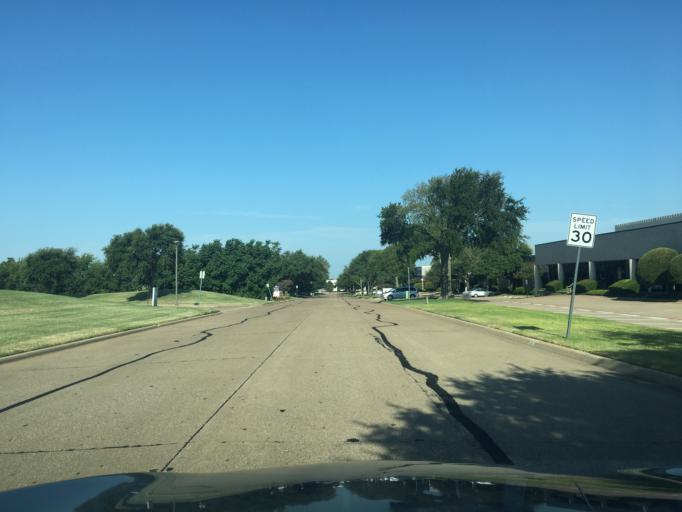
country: US
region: Texas
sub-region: Dallas County
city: Addison
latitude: 32.9651
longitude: -96.8399
